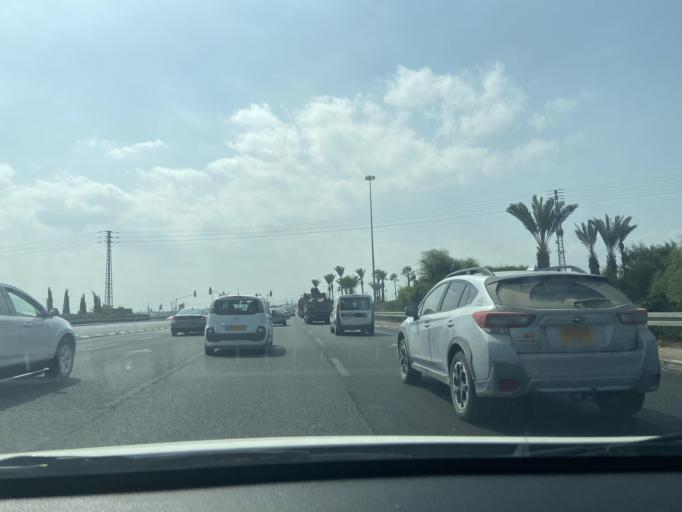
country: IL
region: Northern District
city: `Akko
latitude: 32.9202
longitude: 35.0969
